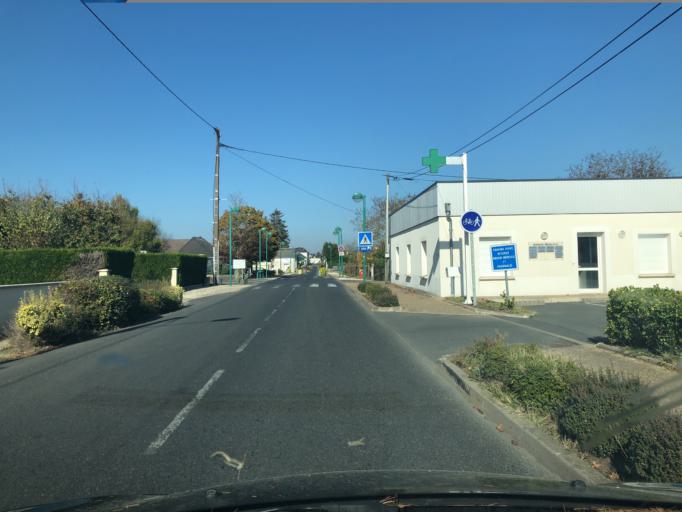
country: FR
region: Centre
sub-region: Departement d'Indre-et-Loire
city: Rouziers-de-Touraine
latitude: 47.5138
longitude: 0.6493
